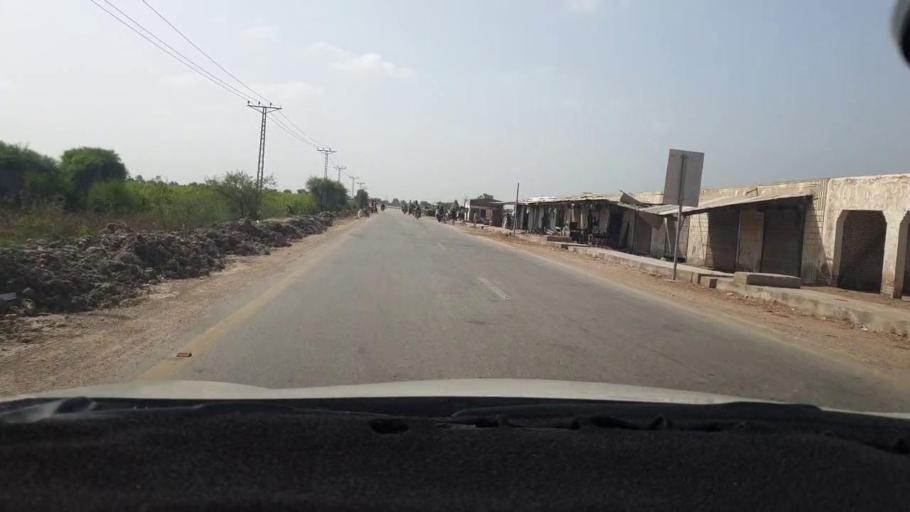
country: PK
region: Sindh
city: Mirpur Khas
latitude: 25.7706
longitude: 69.0713
